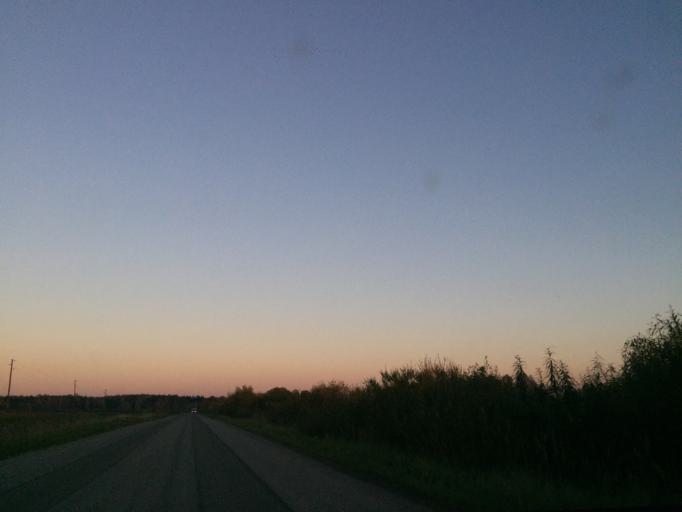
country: LT
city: Vieksniai
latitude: 56.4005
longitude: 22.5405
